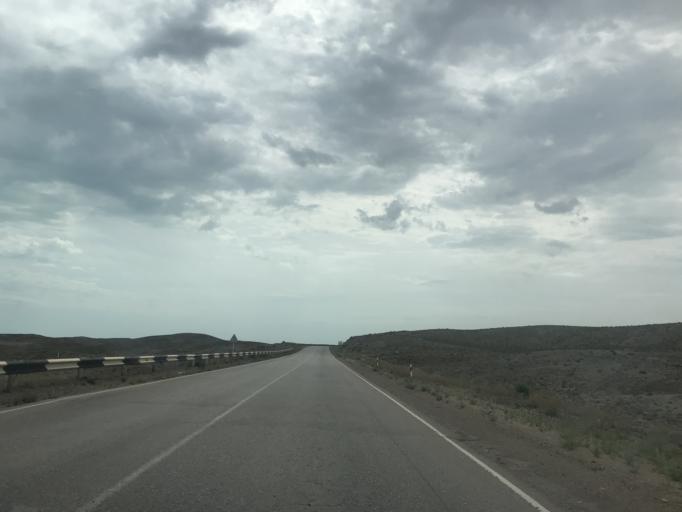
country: KZ
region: Zhambyl
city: Mynaral
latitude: 45.5064
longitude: 73.5042
